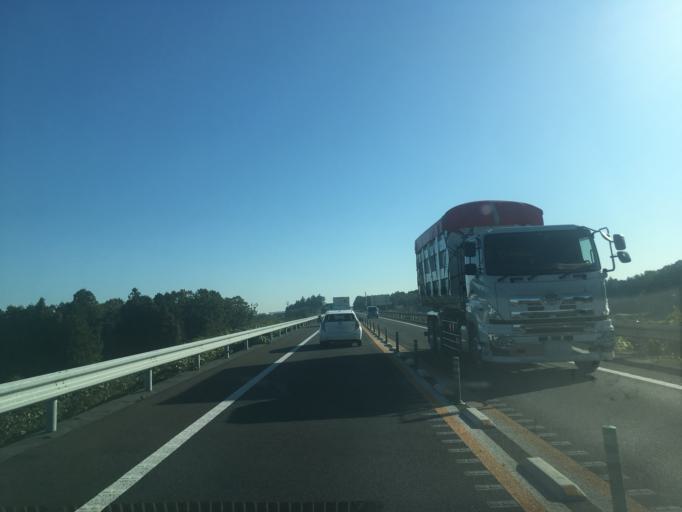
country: JP
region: Ibaraki
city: Mitsukaido
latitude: 36.0567
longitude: 140.0707
